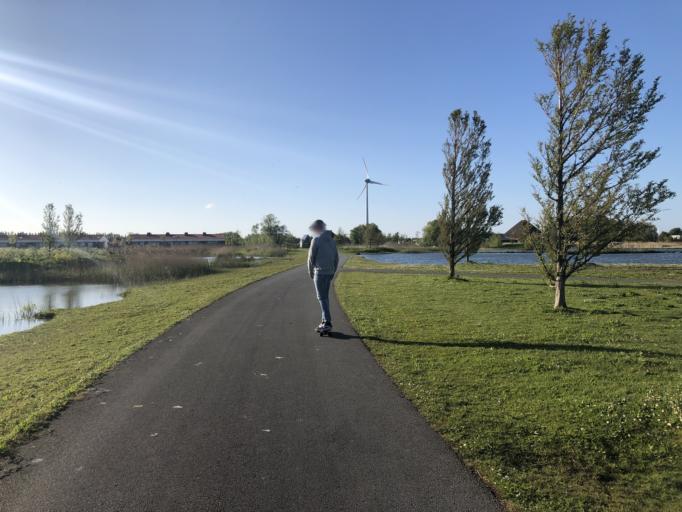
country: NL
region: North Holland
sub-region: Gemeente Langedijk
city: Broek op Langedijk
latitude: 52.6407
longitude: 4.7985
